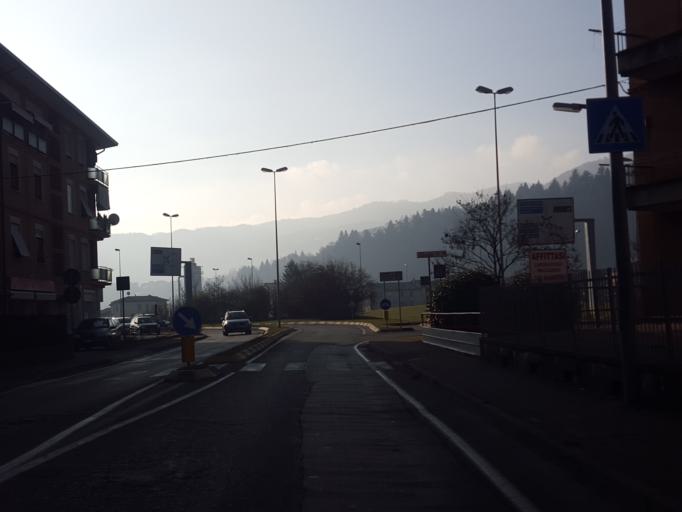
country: IT
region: Veneto
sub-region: Provincia di Vicenza
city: Valdagno
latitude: 45.6334
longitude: 11.3075
